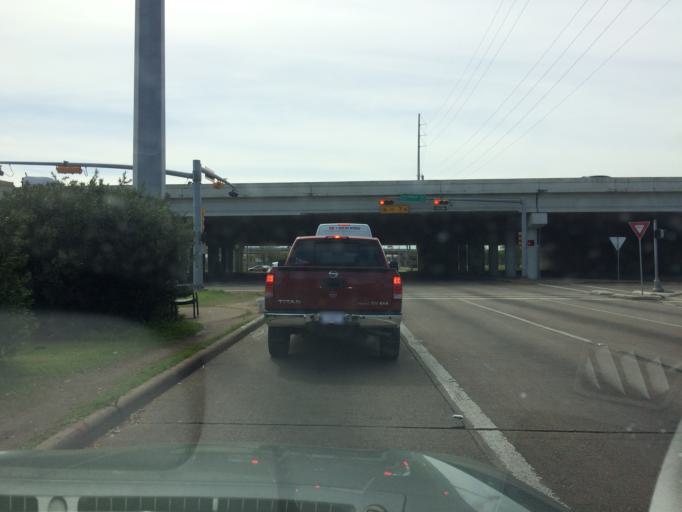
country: US
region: Texas
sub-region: Harris County
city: Bellaire
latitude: 29.7265
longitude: -95.4842
